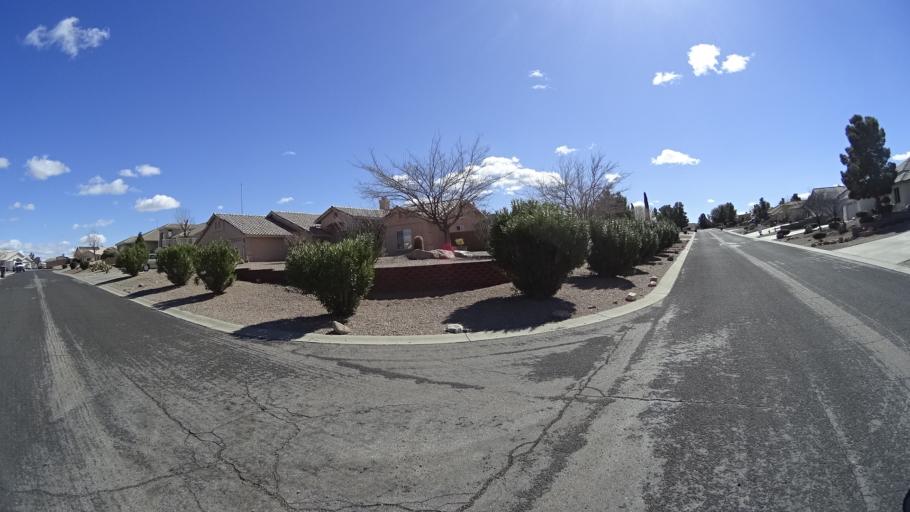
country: US
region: Arizona
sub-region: Mohave County
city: Kingman
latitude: 35.2000
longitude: -113.9620
